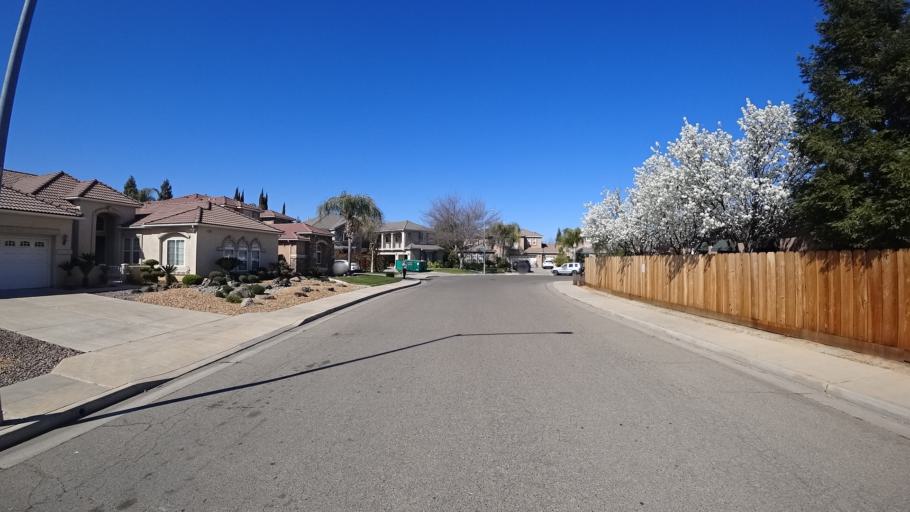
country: US
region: California
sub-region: Fresno County
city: Clovis
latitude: 36.8584
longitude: -119.7339
